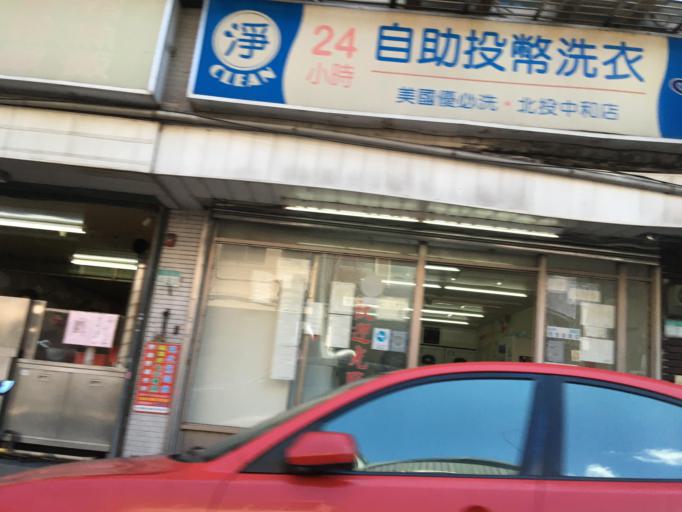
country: TW
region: Taipei
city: Taipei
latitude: 25.1452
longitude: 121.4953
